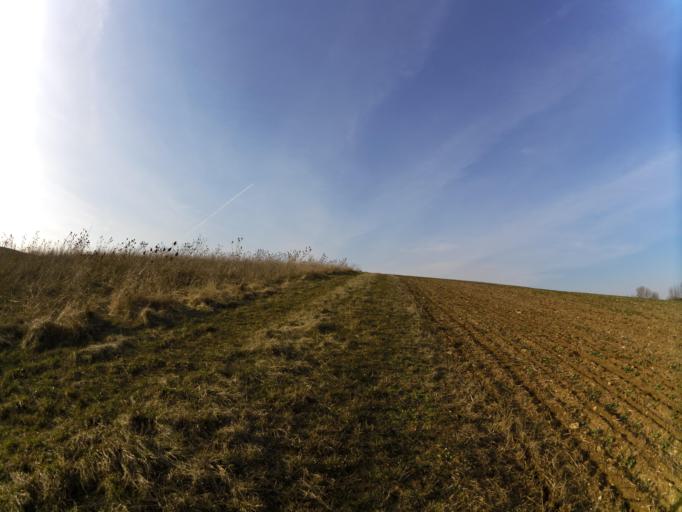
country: DE
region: Bavaria
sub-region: Regierungsbezirk Unterfranken
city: Dettelbach
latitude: 49.8320
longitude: 10.1460
